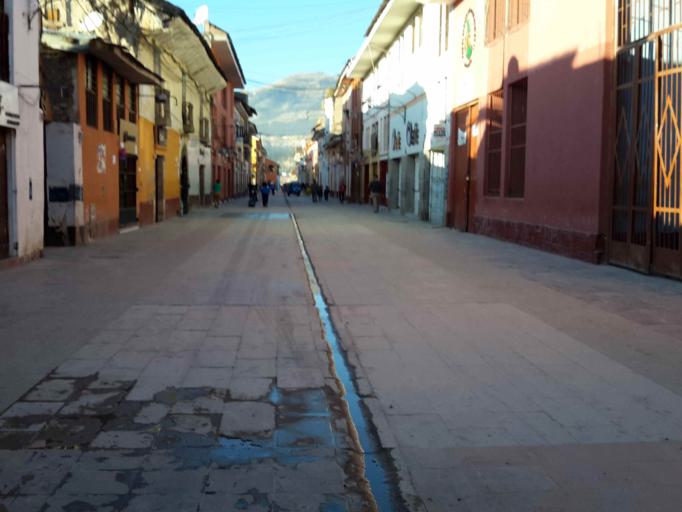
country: PE
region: Ayacucho
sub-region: Provincia de Huamanga
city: Ayacucho
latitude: -13.1577
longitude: -74.2246
